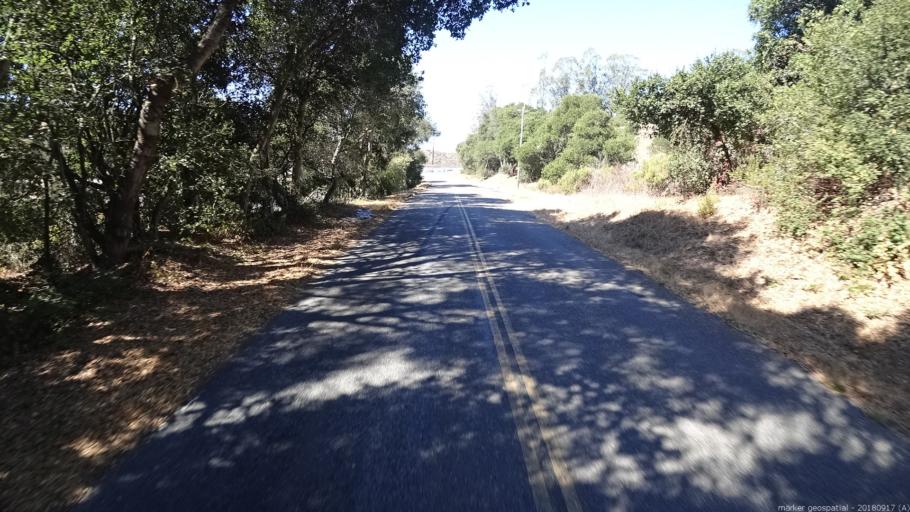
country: US
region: California
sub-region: Monterey County
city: Elkhorn
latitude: 36.8305
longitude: -121.7329
